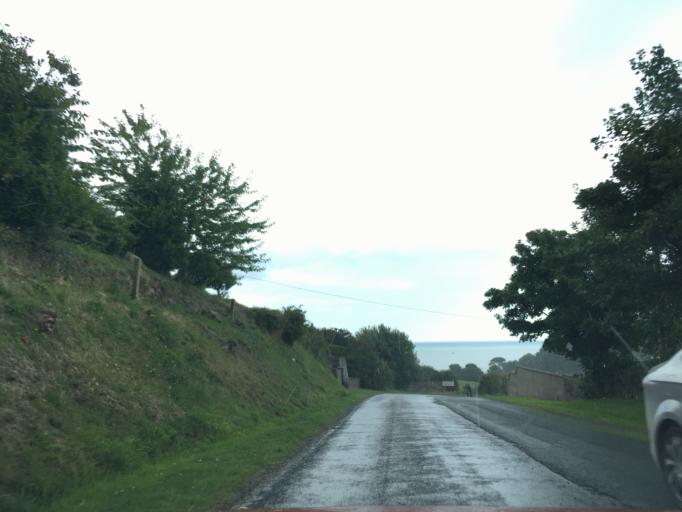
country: IE
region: Munster
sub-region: County Cork
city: Crosshaven
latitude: 51.7842
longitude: -8.3029
